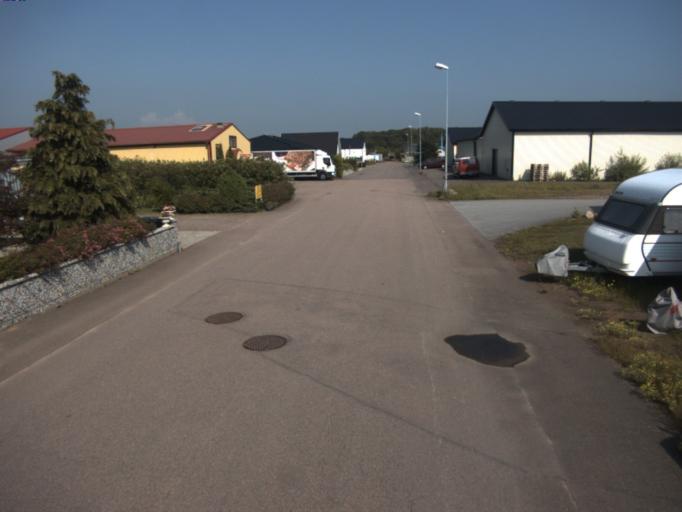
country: SE
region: Skane
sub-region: Helsingborg
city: Odakra
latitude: 56.1101
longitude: 12.7554
